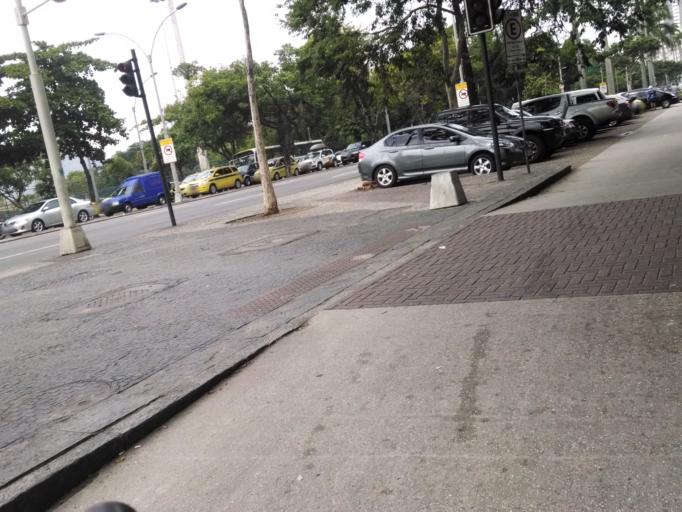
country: BR
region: Rio de Janeiro
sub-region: Rio De Janeiro
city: Rio de Janeiro
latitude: -22.9255
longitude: -43.1730
